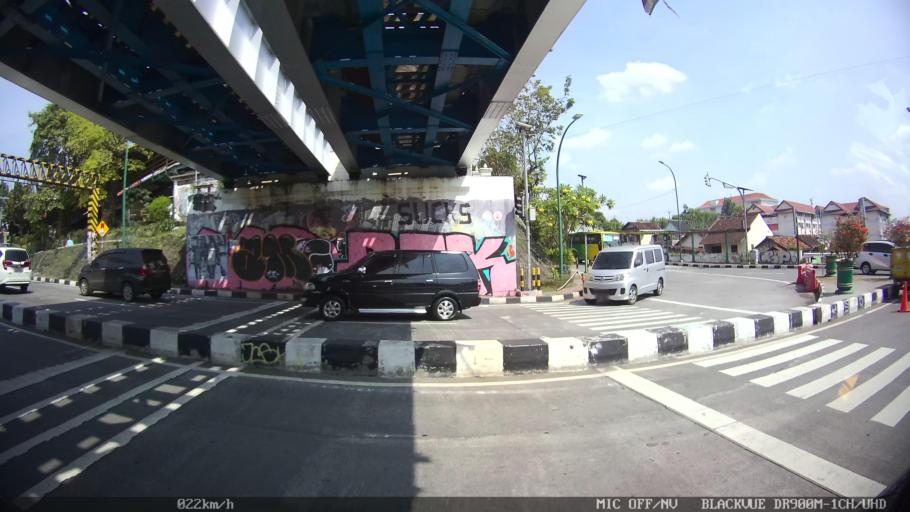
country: ID
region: Daerah Istimewa Yogyakarta
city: Yogyakarta
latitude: -7.7893
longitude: 110.3682
